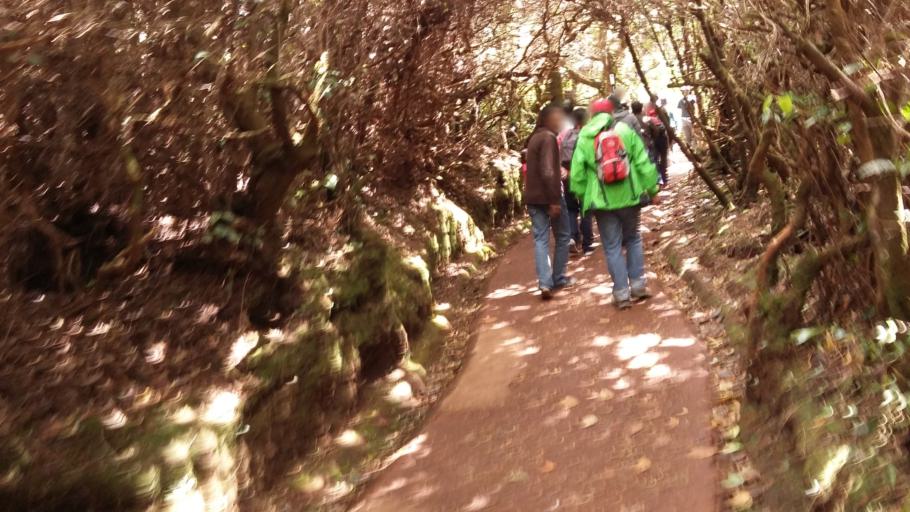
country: CR
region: Alajuela
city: Rio Segundo
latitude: 10.1898
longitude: -84.2323
